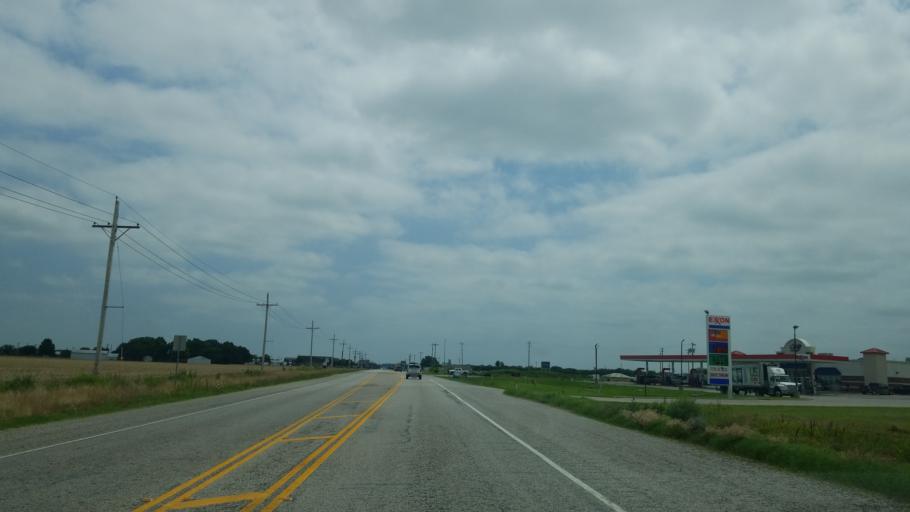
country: US
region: Texas
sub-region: Denton County
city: Pilot Point
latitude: 33.4146
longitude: -96.9402
